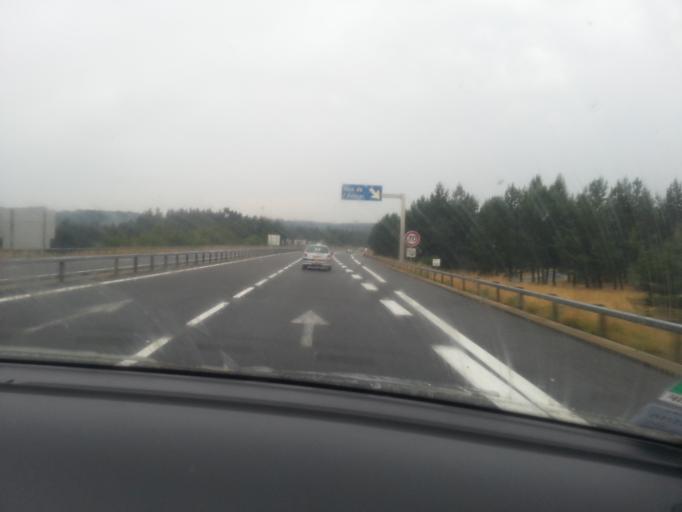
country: FR
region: Languedoc-Roussillon
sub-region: Departement de la Lozere
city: Aumont-Aubrac
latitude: 44.7422
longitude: 3.2884
